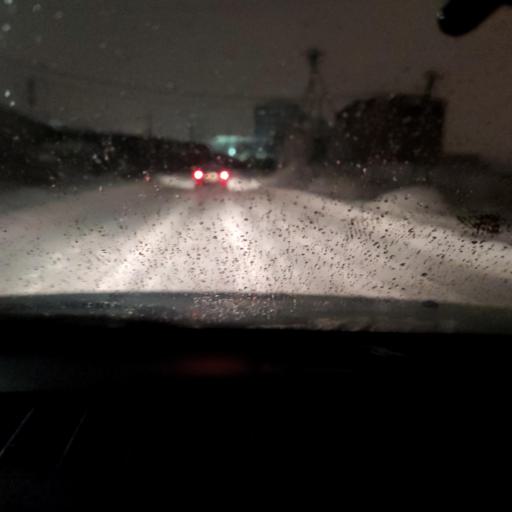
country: RU
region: Perm
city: Kondratovo
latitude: 58.0196
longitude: 56.1371
